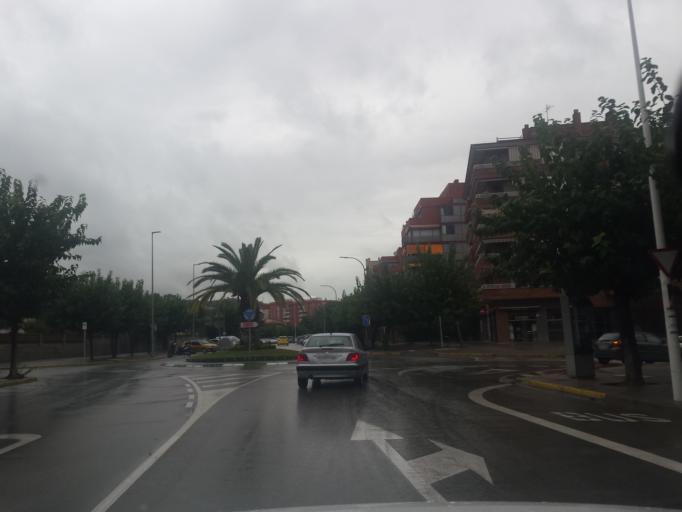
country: ES
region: Catalonia
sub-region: Provincia de Barcelona
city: Sant Andreu de la Barca
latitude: 41.4518
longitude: 1.9623
